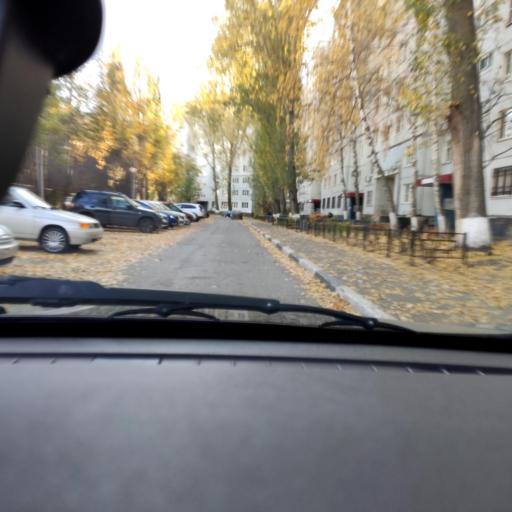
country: RU
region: Samara
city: Tol'yatti
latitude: 53.5318
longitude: 49.3242
